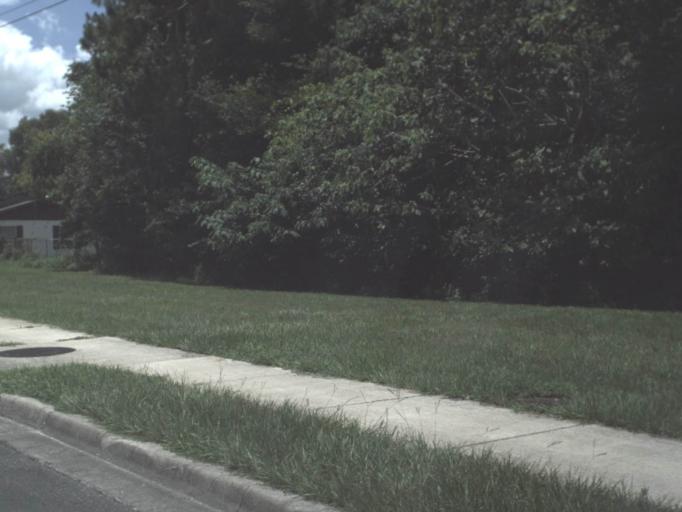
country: US
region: Florida
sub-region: Alachua County
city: Newberry
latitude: 29.6469
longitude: -82.6040
